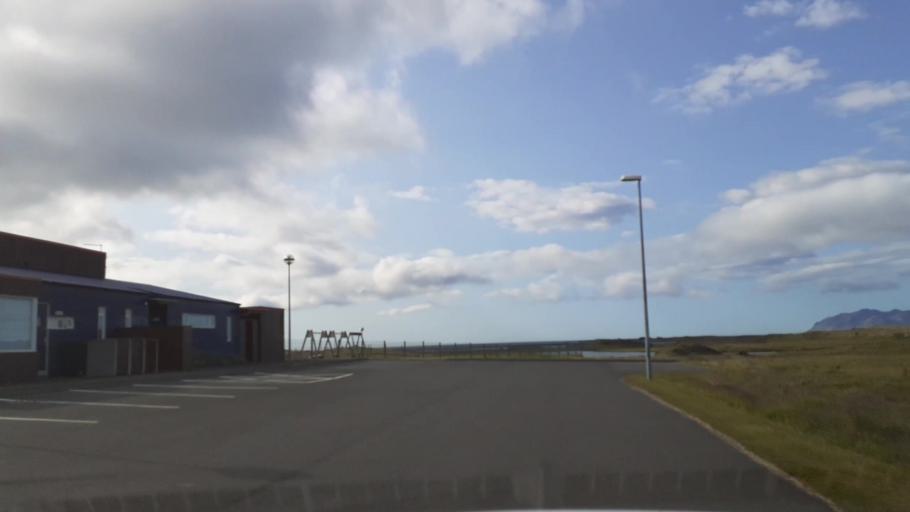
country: IS
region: East
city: Reydarfjoerdur
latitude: 64.6535
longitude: -14.2809
